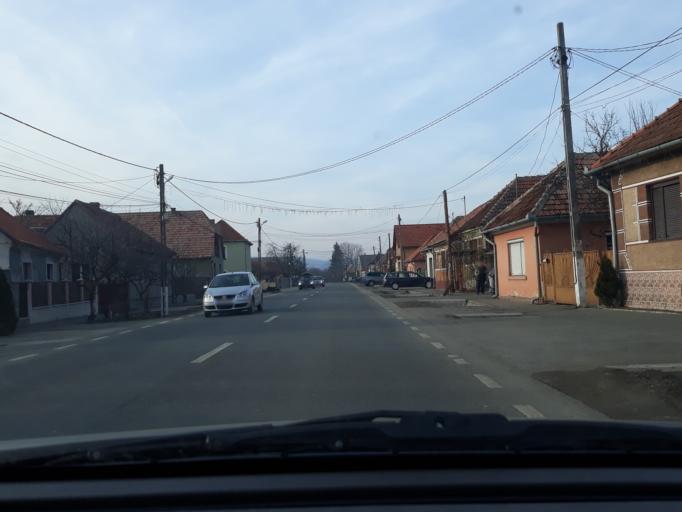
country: RO
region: Salaj
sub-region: Comuna Varsolt
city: Varsolt
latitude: 47.2097
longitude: 22.9099
